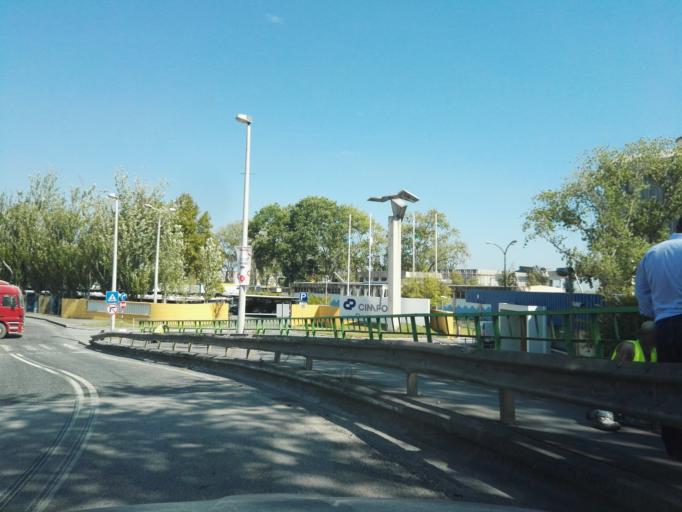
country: PT
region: Lisbon
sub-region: Vila Franca de Xira
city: Alhandra
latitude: 38.9243
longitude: -9.0098
